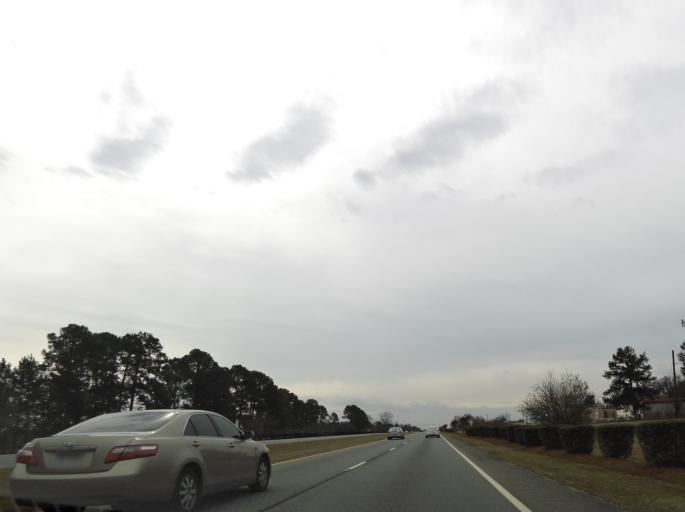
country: US
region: Georgia
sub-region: Houston County
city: Warner Robins
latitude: 32.6264
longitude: -83.6019
